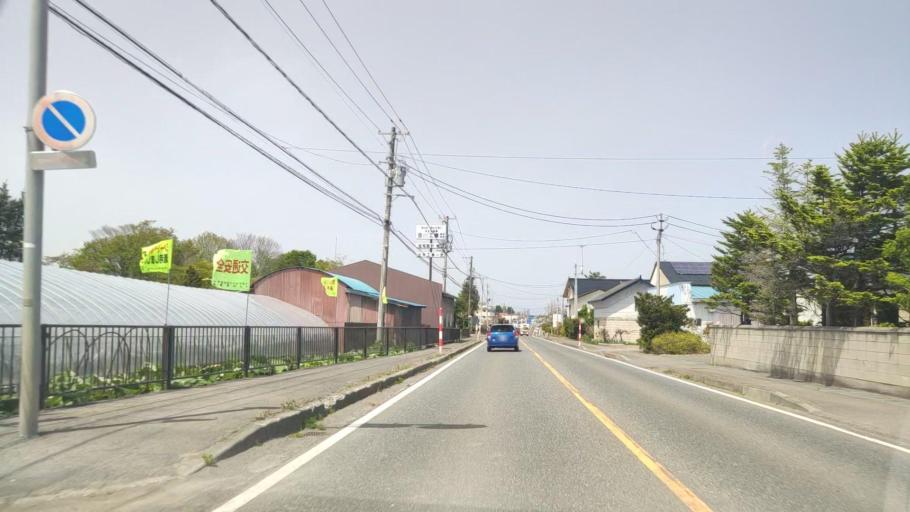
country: JP
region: Aomori
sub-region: Misawa Shi
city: Inuotose
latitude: 40.6529
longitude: 141.1946
